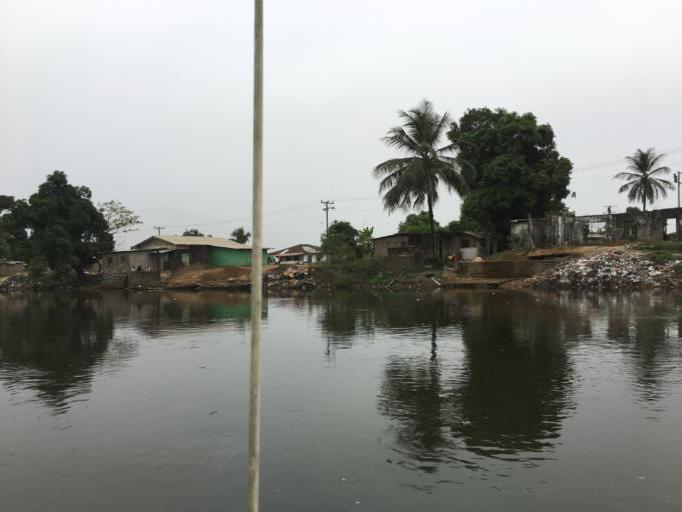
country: LR
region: Montserrado
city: Monrovia
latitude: 6.3710
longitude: -10.7782
